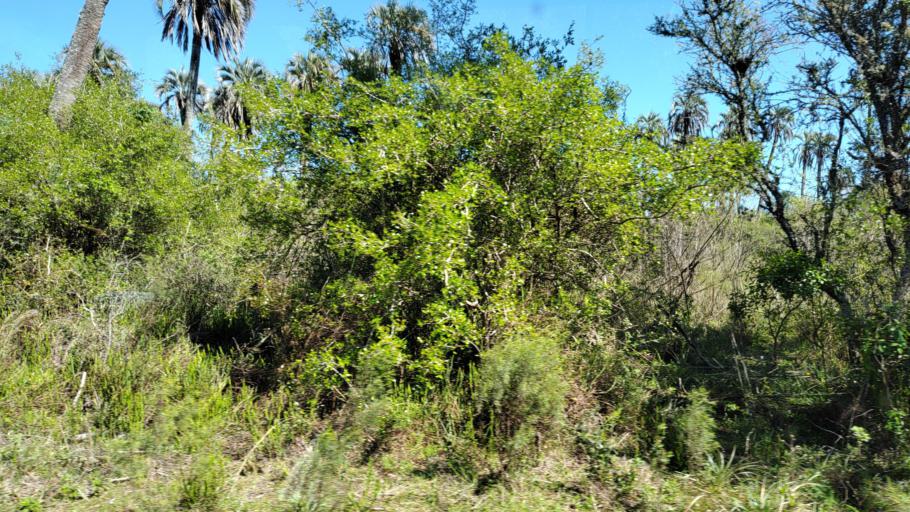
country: AR
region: Entre Rios
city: Ubajay
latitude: -31.8895
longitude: -58.2422
